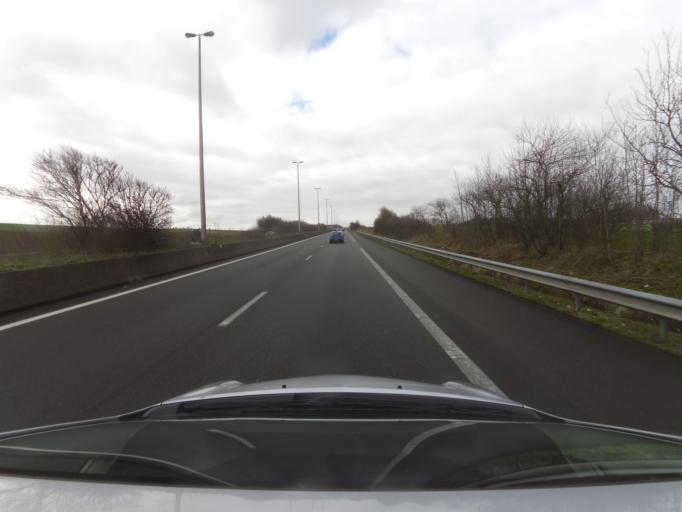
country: FR
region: Nord-Pas-de-Calais
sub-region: Departement du Pas-de-Calais
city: Sangatte
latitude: 50.8908
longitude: 1.7589
